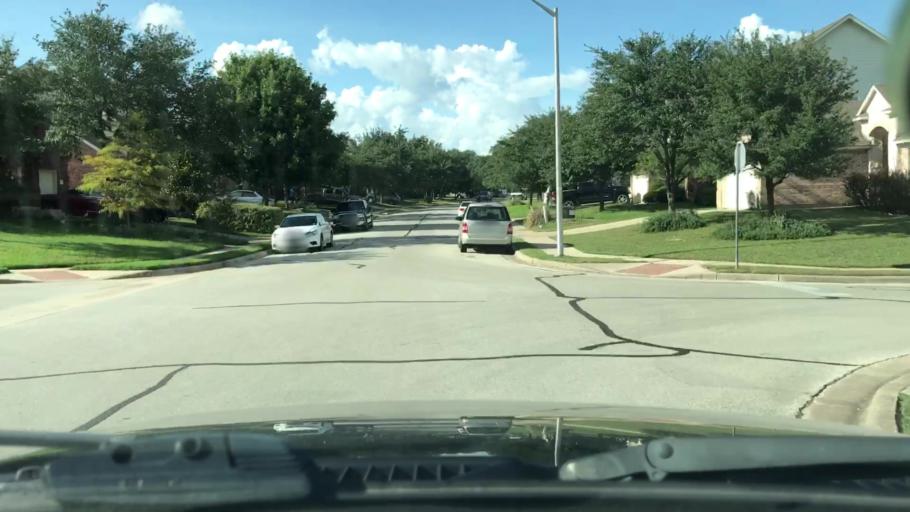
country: US
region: Texas
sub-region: Williamson County
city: Leander
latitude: 30.5420
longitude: -97.8535
